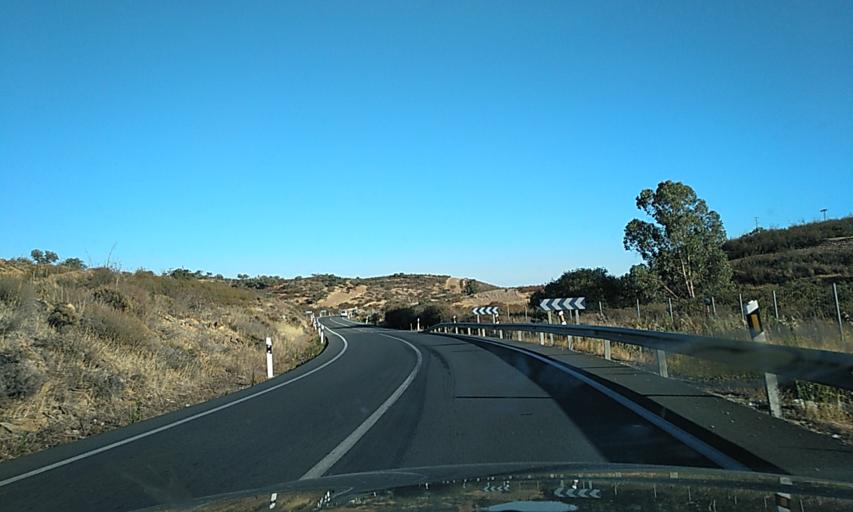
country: ES
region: Andalusia
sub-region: Provincia de Huelva
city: San Bartolome de la Torre
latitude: 37.4845
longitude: -7.1303
